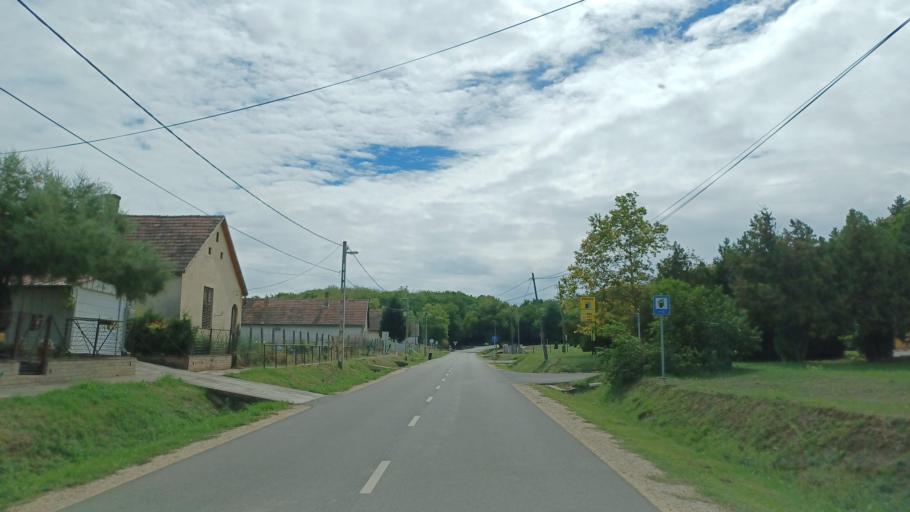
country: HU
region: Tolna
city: Zomba
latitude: 46.4984
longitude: 18.5917
